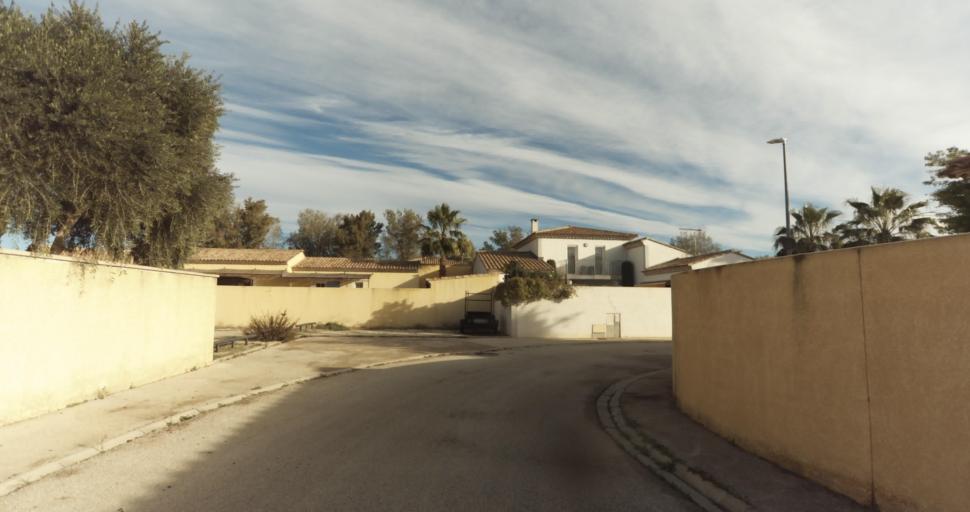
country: FR
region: Languedoc-Roussillon
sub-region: Departement du Gard
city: Aigues-Mortes
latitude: 43.5675
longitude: 4.2064
